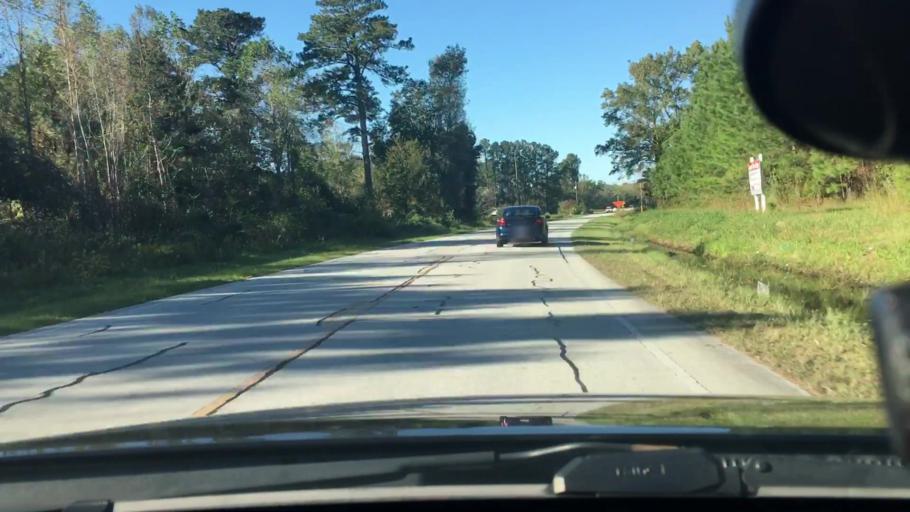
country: US
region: North Carolina
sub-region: Craven County
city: Vanceboro
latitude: 35.2839
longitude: -77.1542
